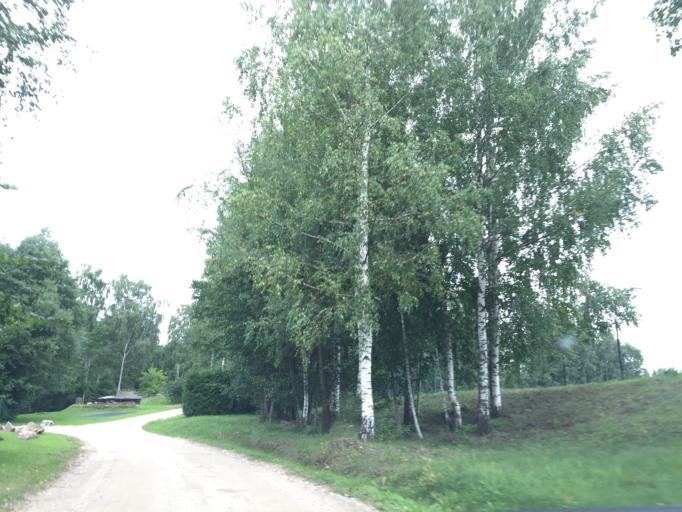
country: LV
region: Kegums
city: Kegums
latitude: 56.7475
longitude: 24.7099
